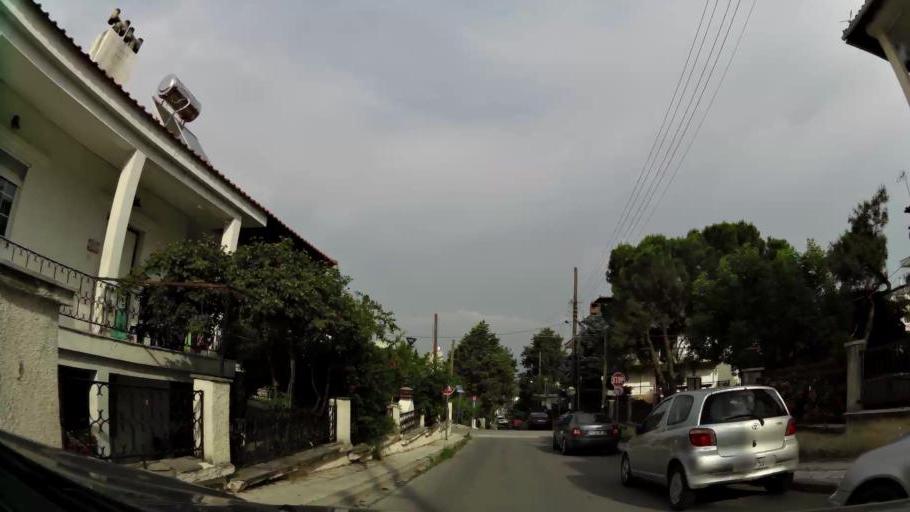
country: GR
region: Central Macedonia
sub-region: Nomos Thessalonikis
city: Oraiokastro
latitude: 40.7298
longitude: 22.9172
